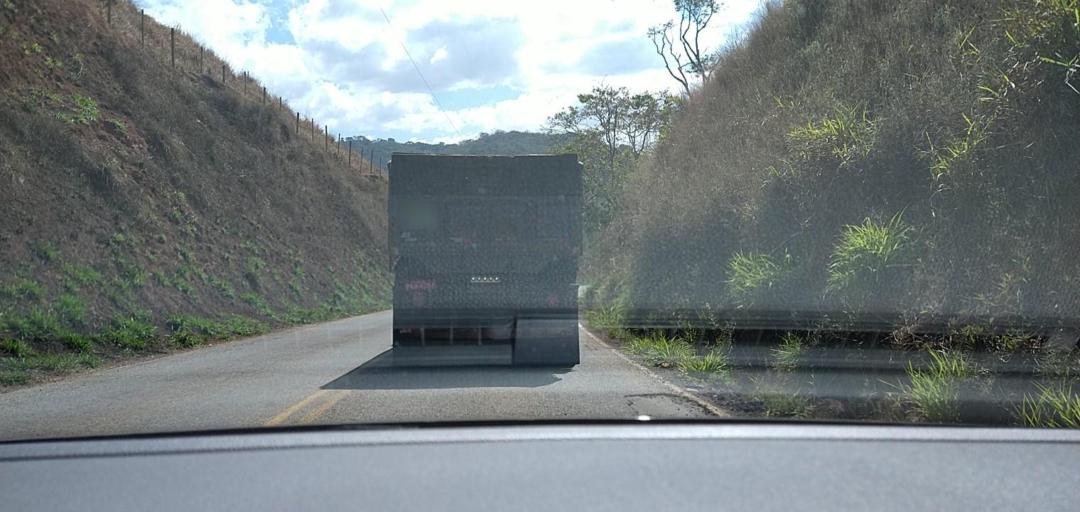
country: BR
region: Minas Gerais
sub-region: Ponte Nova
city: Ponte Nova
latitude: -20.2838
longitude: -42.9021
